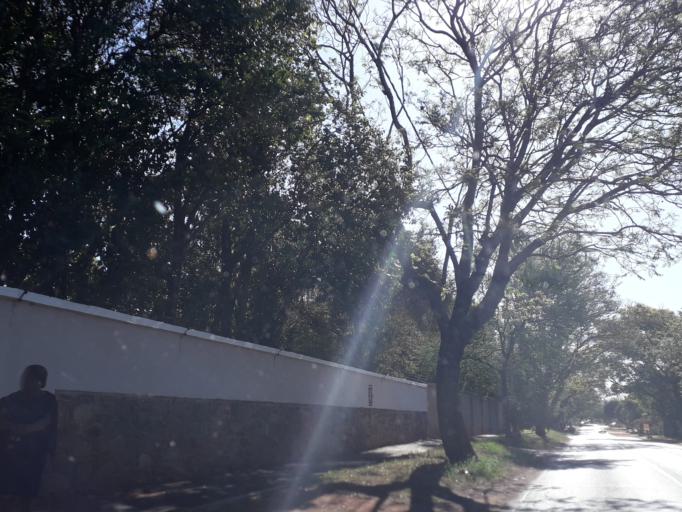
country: ZA
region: Gauteng
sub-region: City of Johannesburg Metropolitan Municipality
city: Roodepoort
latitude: -26.1362
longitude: 27.9654
